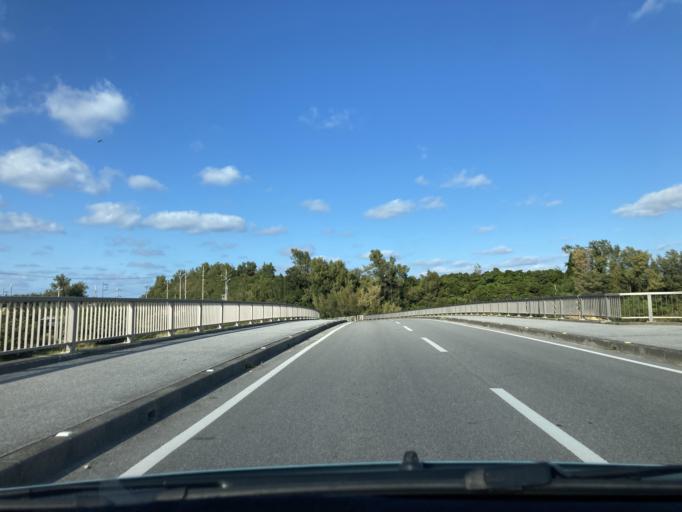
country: JP
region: Okinawa
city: Katsuren-haebaru
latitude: 26.3162
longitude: 127.9182
